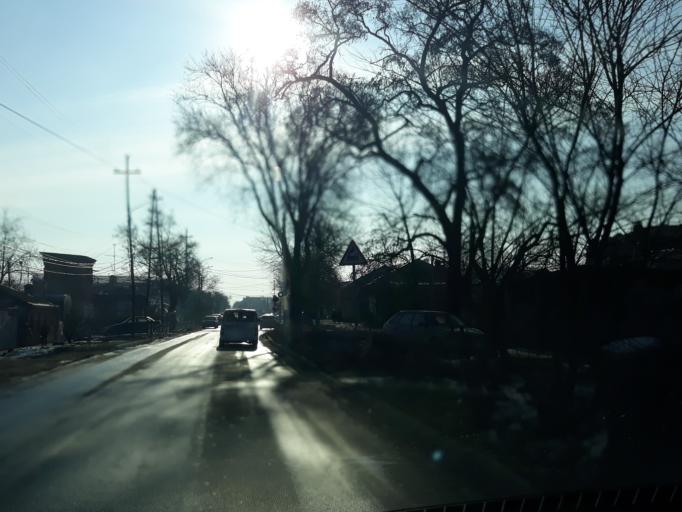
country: RU
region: Rostov
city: Taganrog
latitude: 47.2225
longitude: 38.9143
